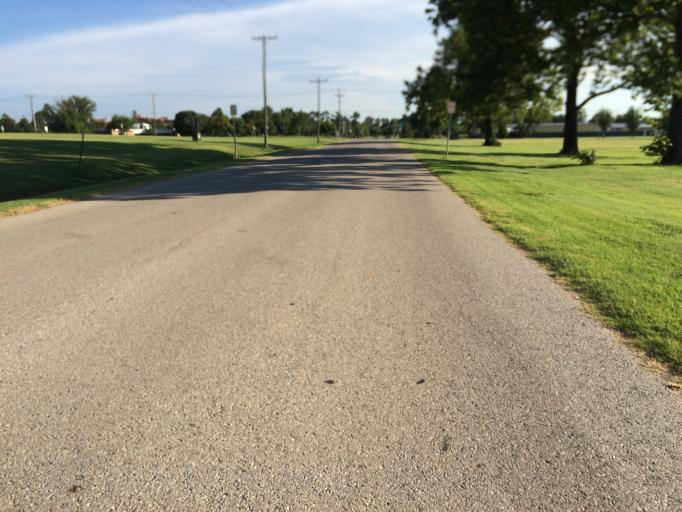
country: US
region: Oklahoma
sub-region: Cleveland County
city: Norman
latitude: 35.1900
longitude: -97.4396
